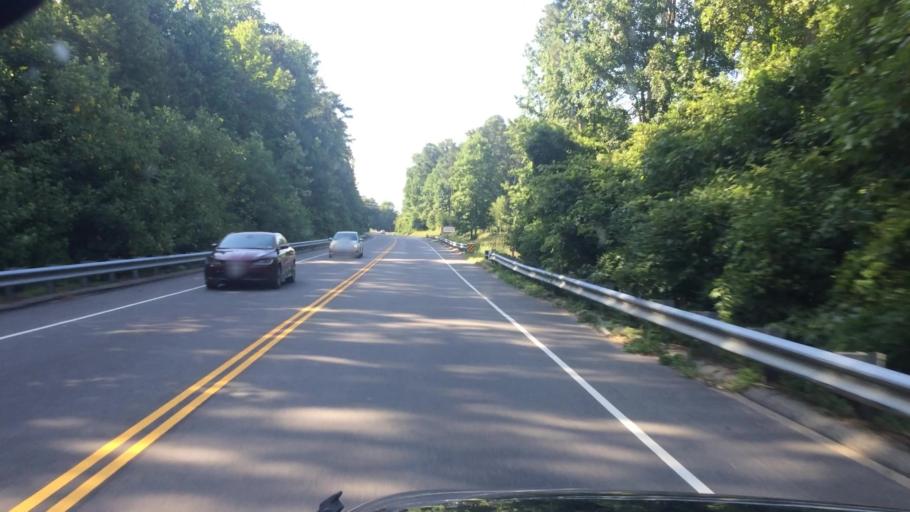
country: US
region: Virginia
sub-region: James City County
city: Williamsburg
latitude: 37.2981
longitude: -76.7249
